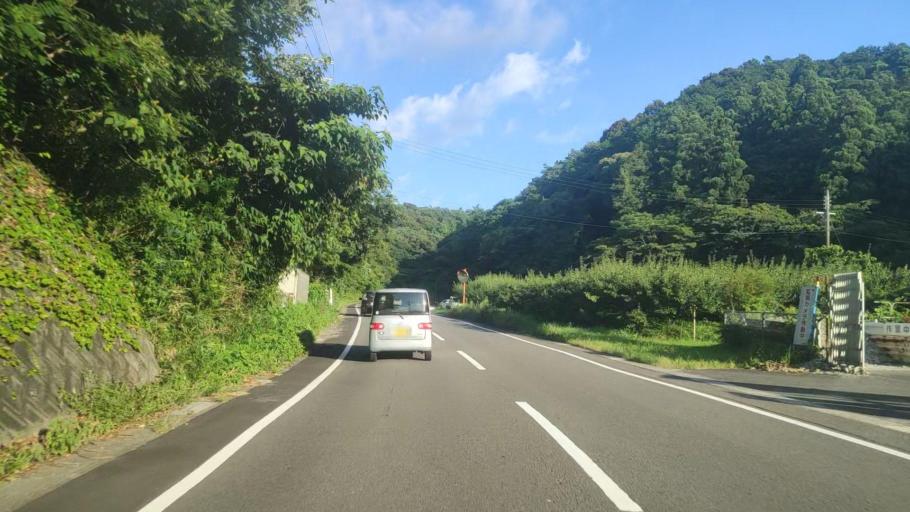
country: JP
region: Wakayama
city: Tanabe
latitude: 33.7320
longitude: 135.4335
